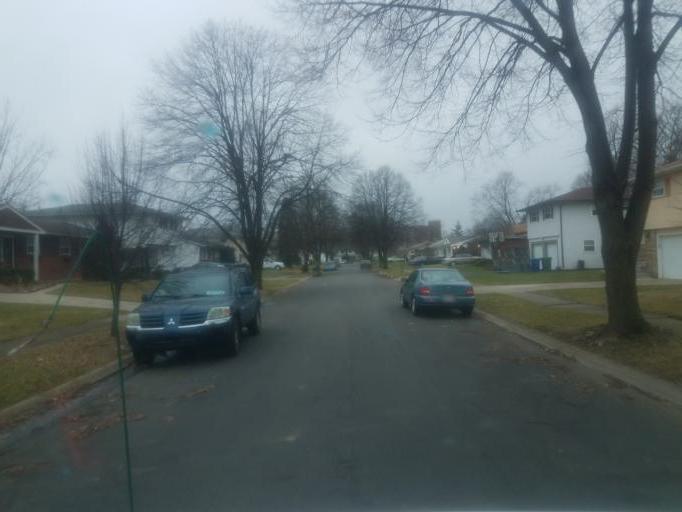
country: US
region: Ohio
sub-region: Franklin County
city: Worthington
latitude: 40.0990
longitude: -82.9811
